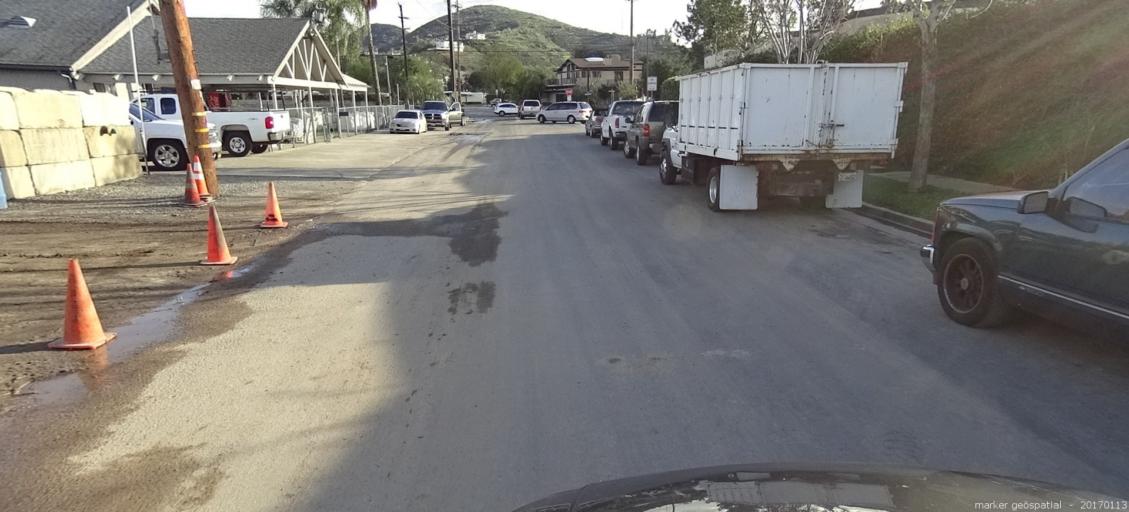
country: US
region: California
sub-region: Orange County
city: Villa Park
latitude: 33.8114
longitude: -117.7982
